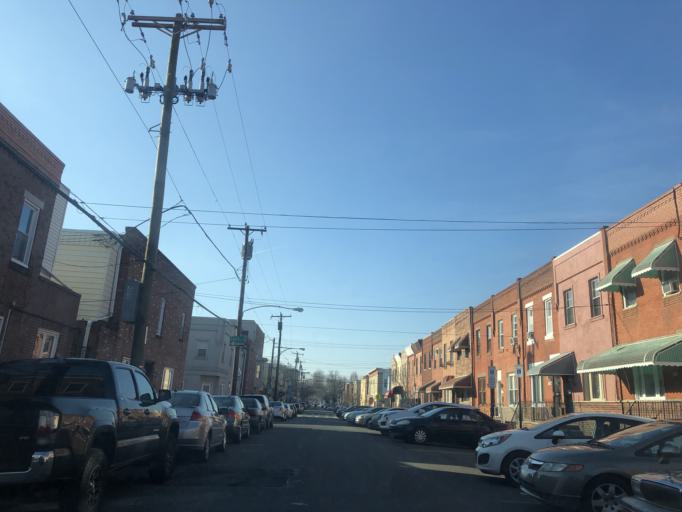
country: US
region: Pennsylvania
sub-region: Philadelphia County
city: Philadelphia
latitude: 39.9217
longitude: -75.1790
